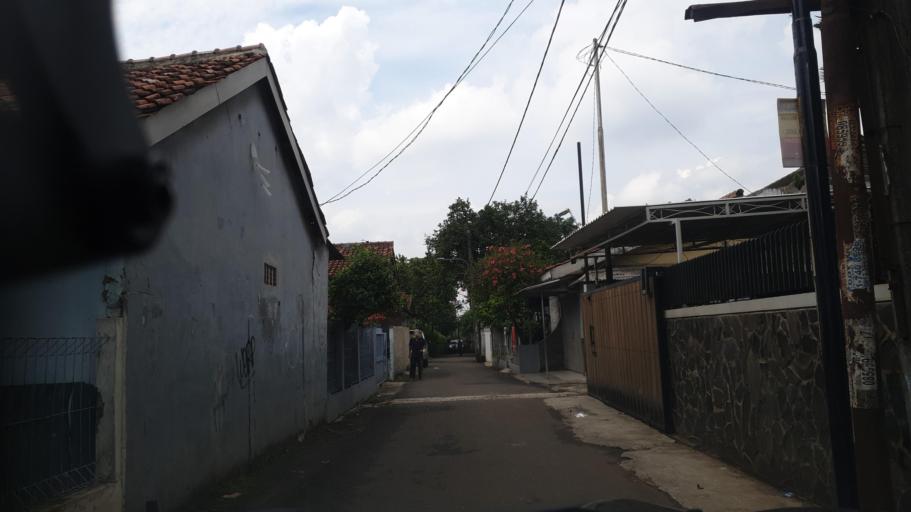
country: ID
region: West Java
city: Pamulang
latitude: -6.3366
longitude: 106.7729
